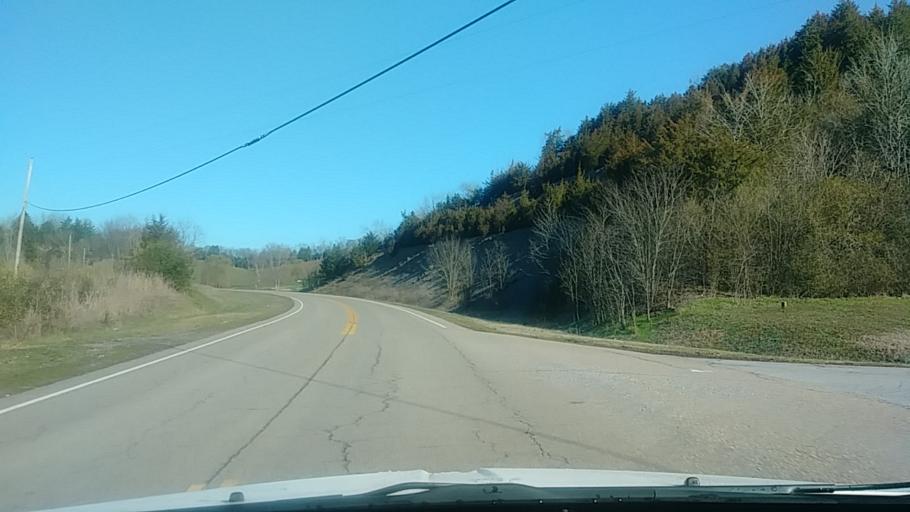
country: US
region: Tennessee
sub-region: Hamblen County
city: Morristown
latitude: 36.1758
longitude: -83.1600
